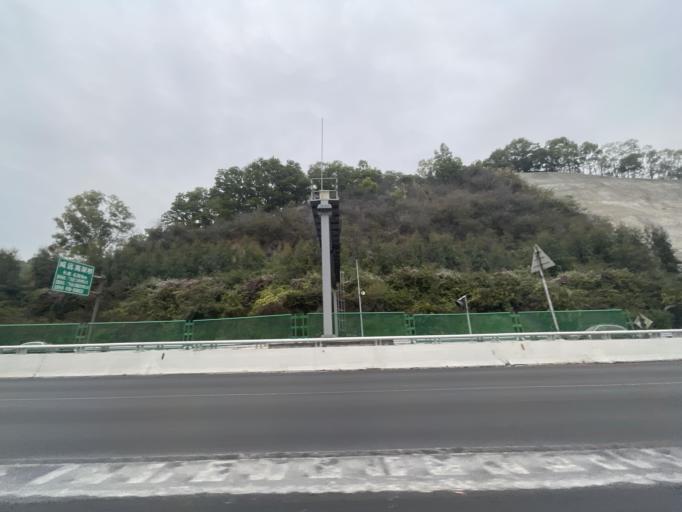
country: CN
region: Guangdong
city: Xinwan
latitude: 22.8025
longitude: 113.6250
